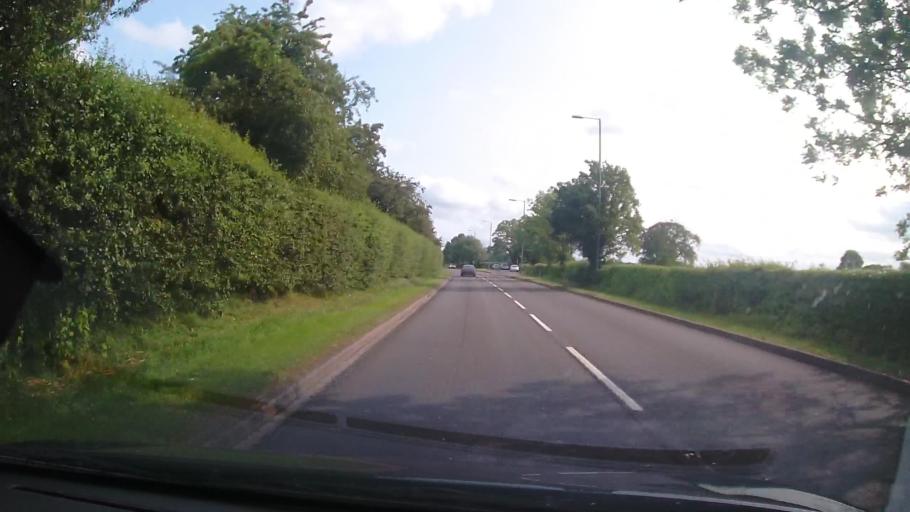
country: GB
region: England
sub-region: Shropshire
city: Shrewsbury
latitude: 52.7404
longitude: -2.7453
